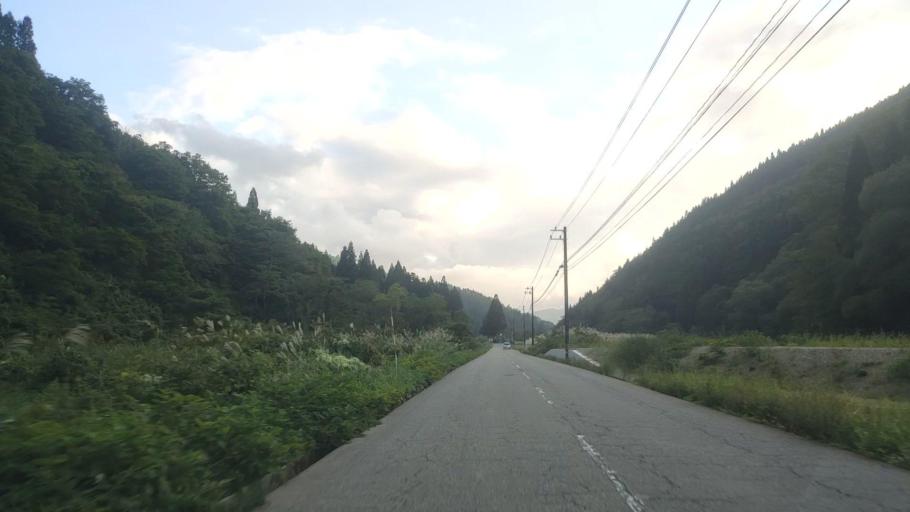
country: JP
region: Toyama
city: Yatsuomachi-higashikumisaka
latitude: 36.4732
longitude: 137.0493
